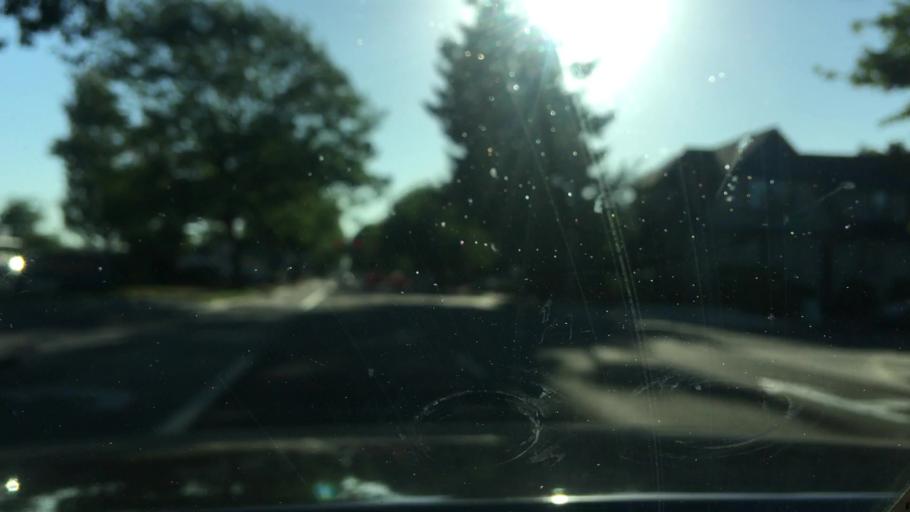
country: US
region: Oregon
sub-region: Lane County
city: Eugene
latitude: 44.0533
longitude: -123.1108
